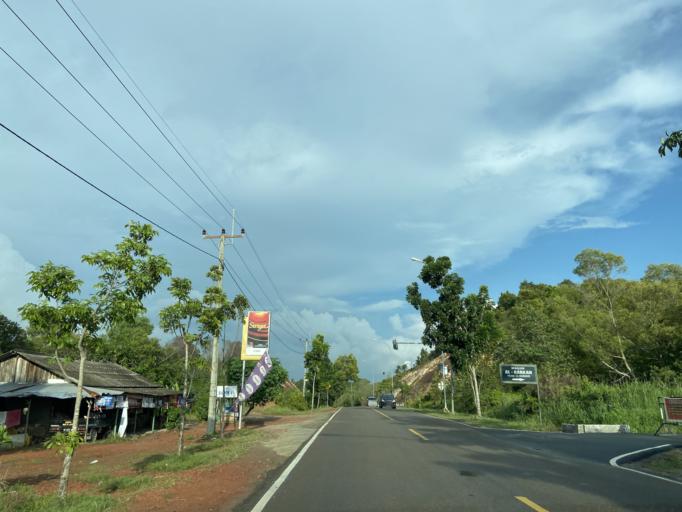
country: ID
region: Riau Islands
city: Tanjungpinang
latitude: 0.9508
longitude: 104.0696
